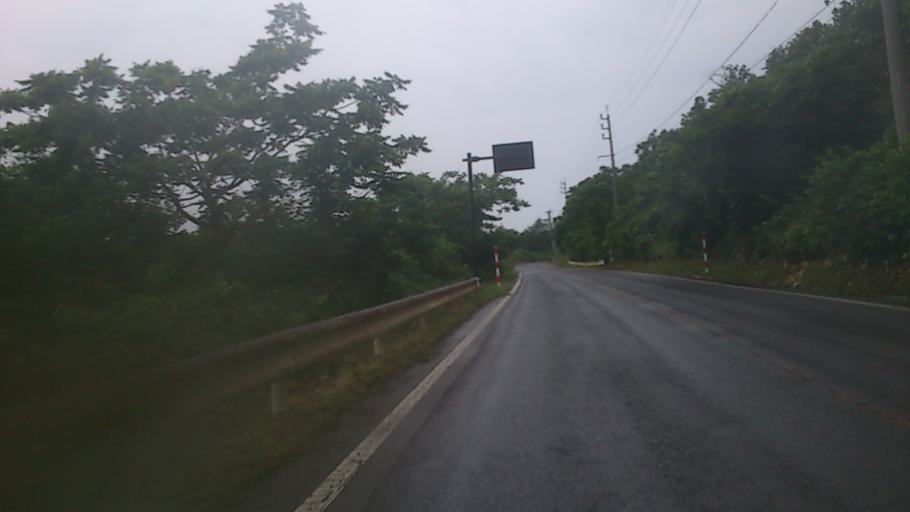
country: JP
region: Akita
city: Noshiromachi
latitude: 40.4244
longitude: 139.9464
